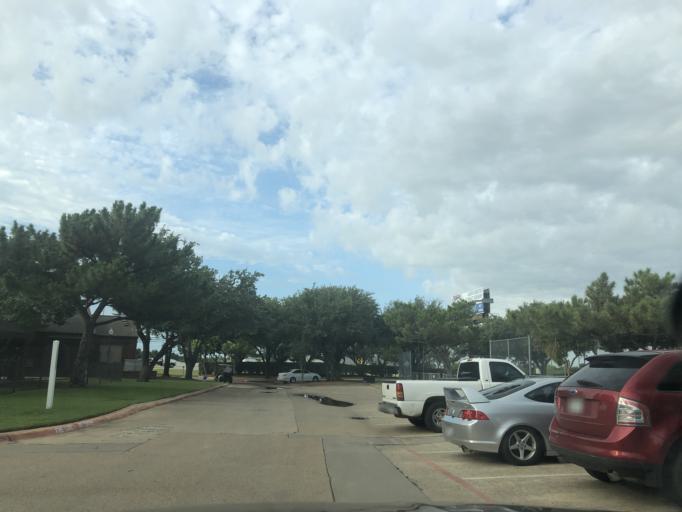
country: US
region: Texas
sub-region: Dallas County
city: Sunnyvale
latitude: 32.8488
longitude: -96.5773
